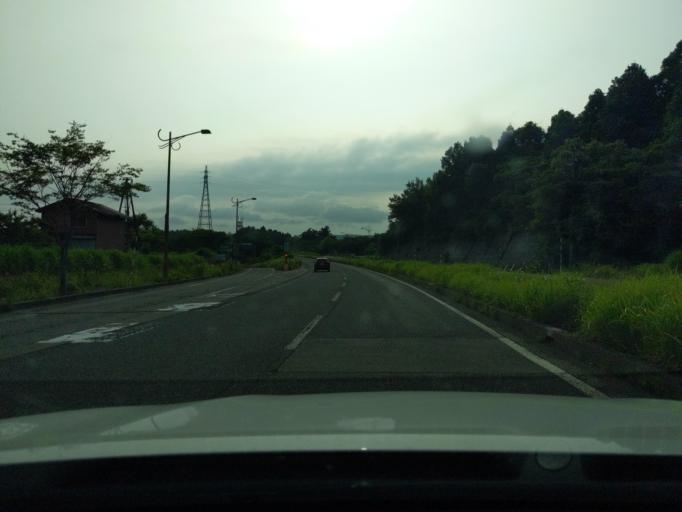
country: JP
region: Niigata
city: Nagaoka
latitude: 37.4508
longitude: 138.7614
